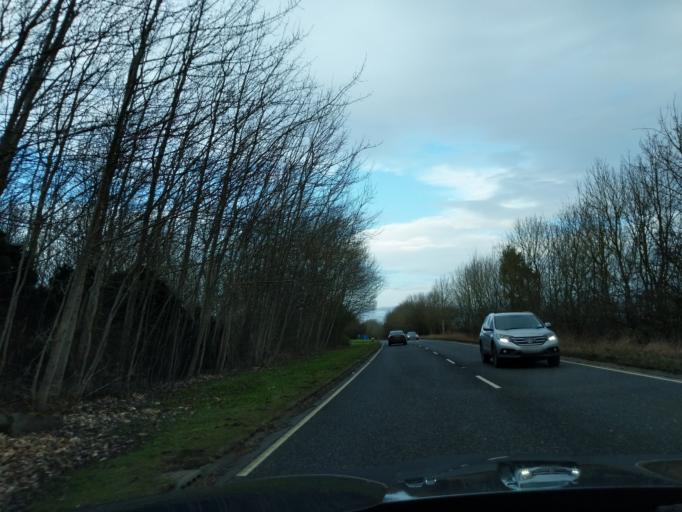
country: GB
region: England
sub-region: Northumberland
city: Meldon
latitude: 55.0879
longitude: -1.8109
